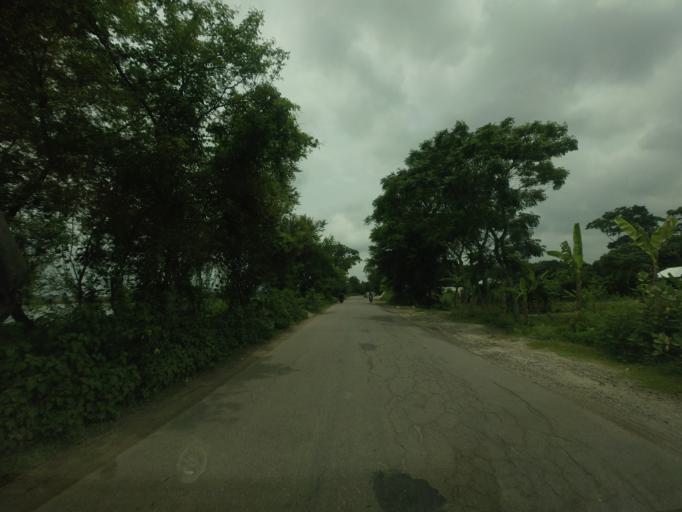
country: BD
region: Khulna
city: Kalia
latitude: 23.2049
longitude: 89.6985
